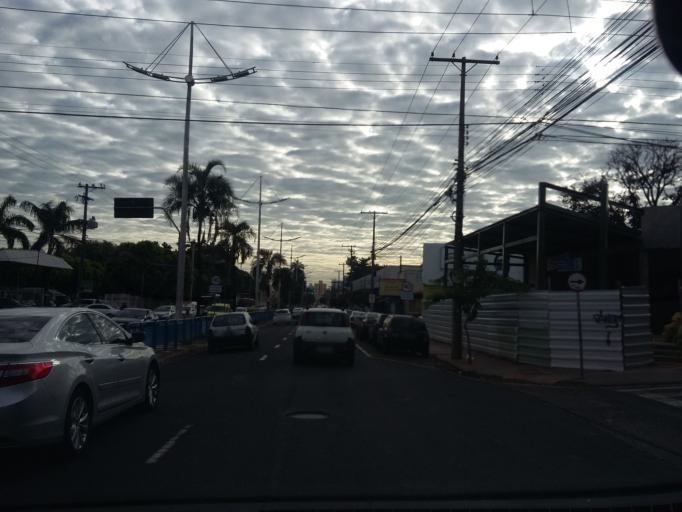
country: BR
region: Sao Paulo
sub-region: Sao Jose Do Rio Preto
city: Sao Jose do Rio Preto
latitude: -20.8295
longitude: -49.3972
